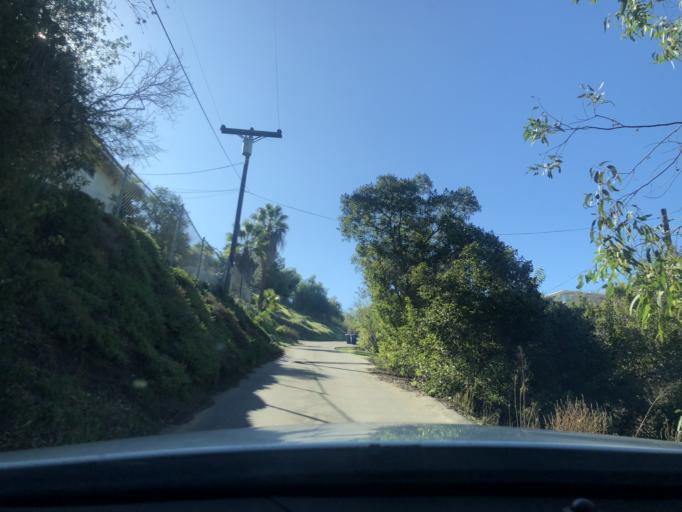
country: US
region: California
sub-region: San Diego County
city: El Cajon
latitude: 32.7771
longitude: -116.9456
